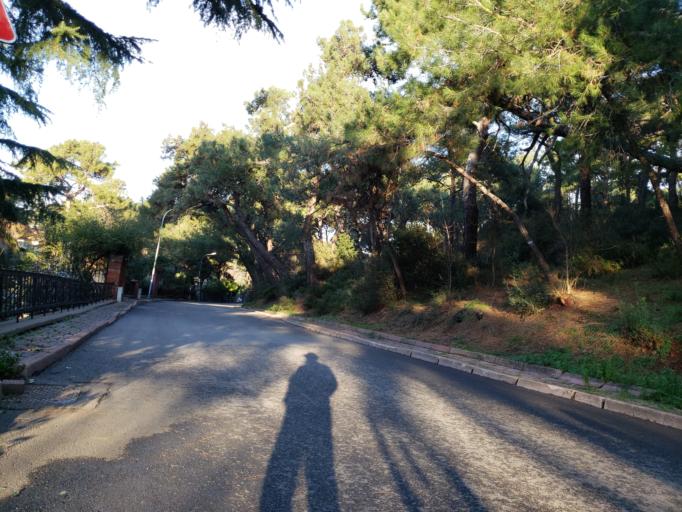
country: TR
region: Istanbul
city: Adalan
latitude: 40.8771
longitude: 29.0881
